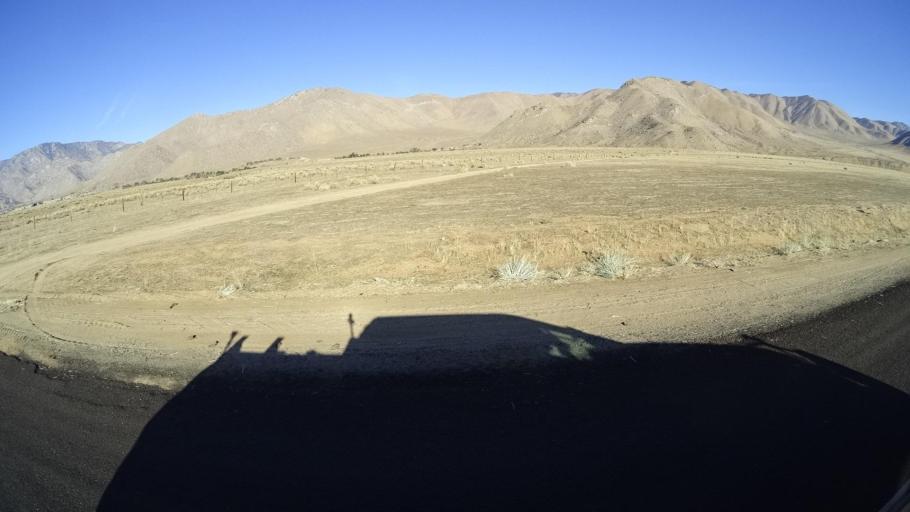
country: US
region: California
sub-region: Kern County
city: Weldon
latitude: 35.6230
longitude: -118.2597
